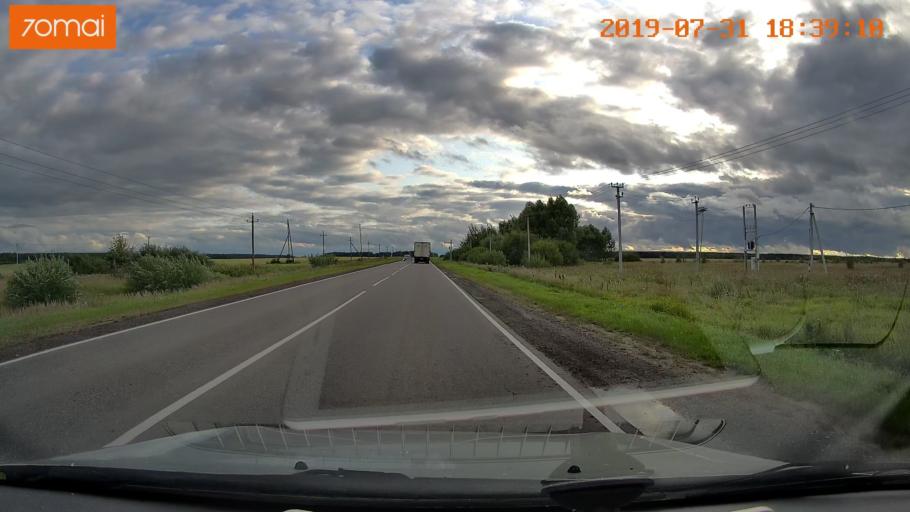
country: RU
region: Moskovskaya
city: Voskresensk
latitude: 55.2691
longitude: 38.6487
